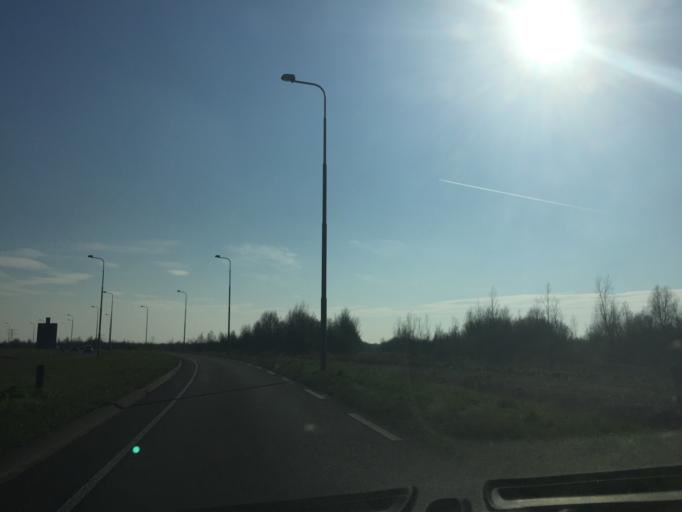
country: NL
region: North Holland
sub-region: Gemeente Bloemendaal
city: Bennebroek
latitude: 52.3040
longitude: 4.6196
